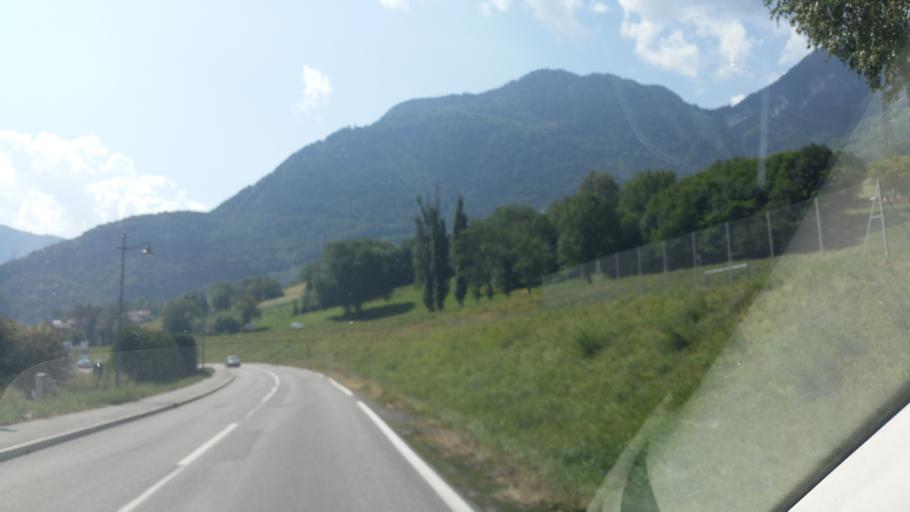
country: FR
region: Rhone-Alpes
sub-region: Departement de la Savoie
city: Aigueblanche
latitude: 45.5043
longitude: 6.4983
